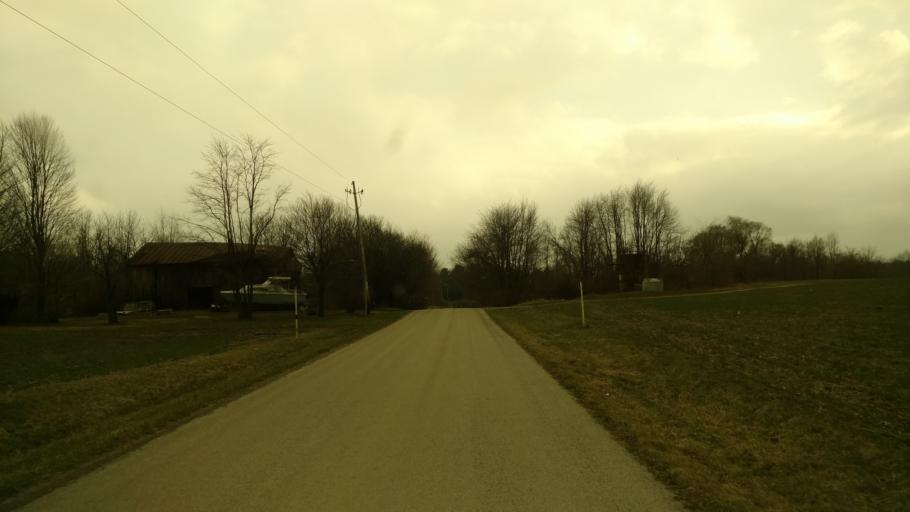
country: US
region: Ohio
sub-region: Morrow County
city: Mount Gilead
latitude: 40.5695
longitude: -82.7718
